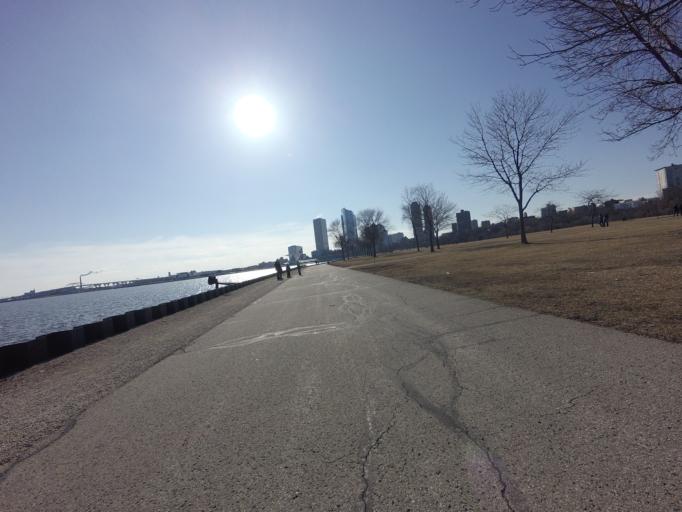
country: US
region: Wisconsin
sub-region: Milwaukee County
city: Milwaukee
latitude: 43.0433
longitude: -87.8879
